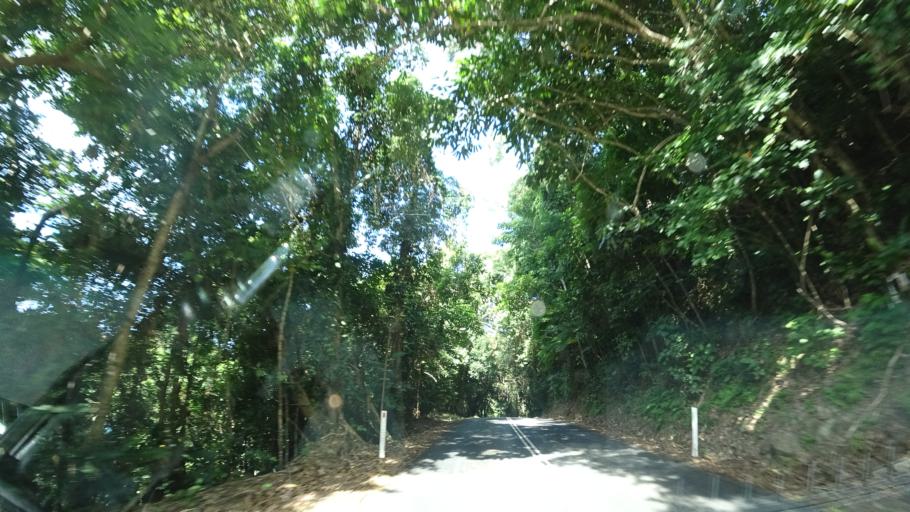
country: AU
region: Queensland
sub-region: Cairns
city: Port Douglas
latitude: -16.1241
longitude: 145.4570
